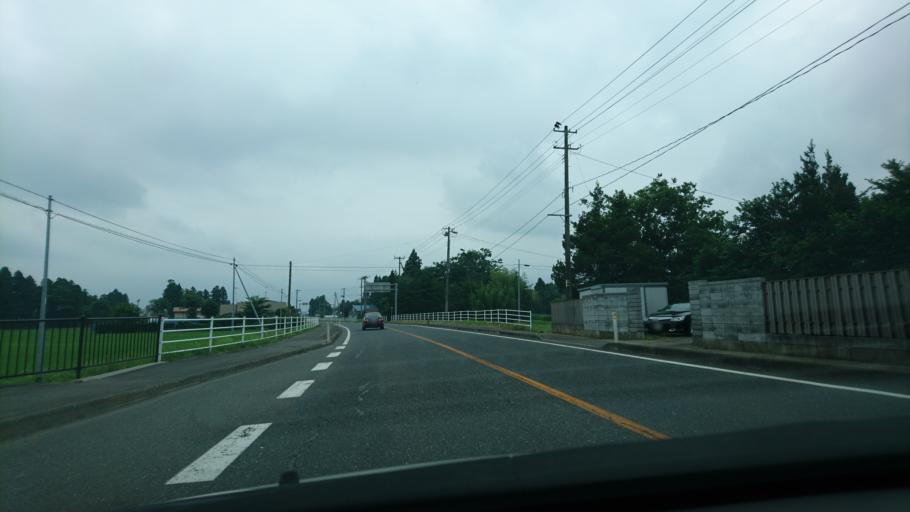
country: JP
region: Miyagi
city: Furukawa
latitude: 38.7010
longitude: 140.8398
